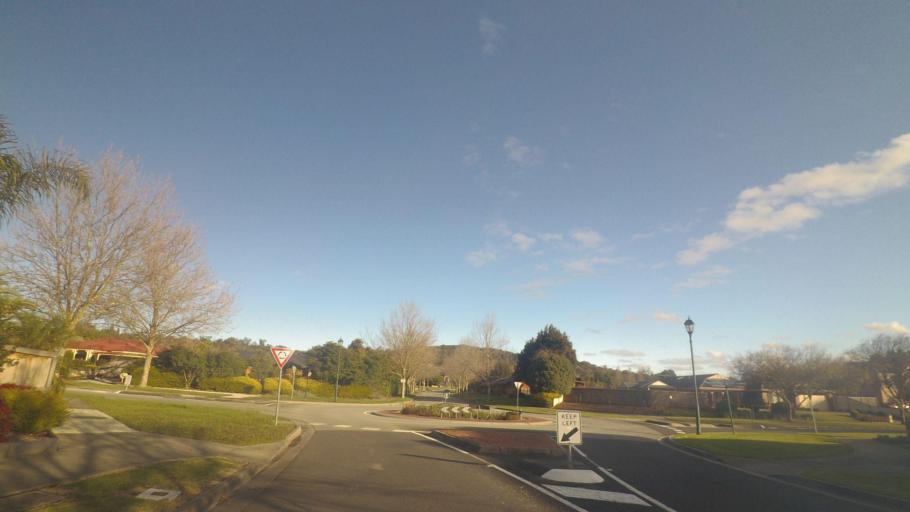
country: AU
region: Victoria
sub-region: Yarra Ranges
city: Lysterfield
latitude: -37.9179
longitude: 145.2870
